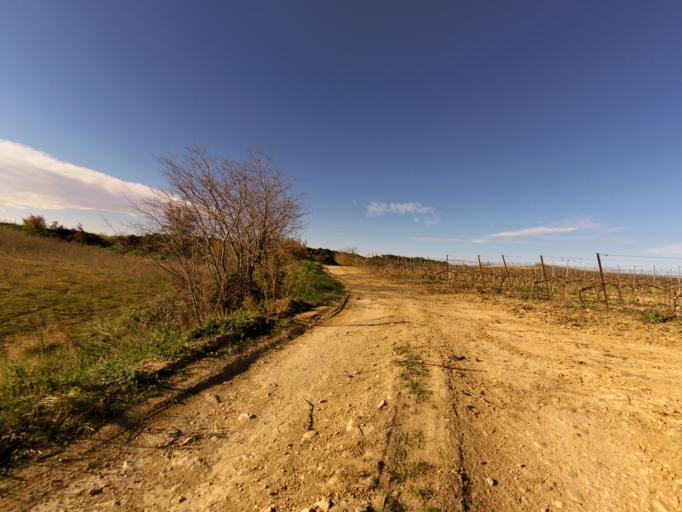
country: FR
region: Languedoc-Roussillon
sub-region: Departement du Gard
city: Mus
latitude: 43.7319
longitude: 4.1977
